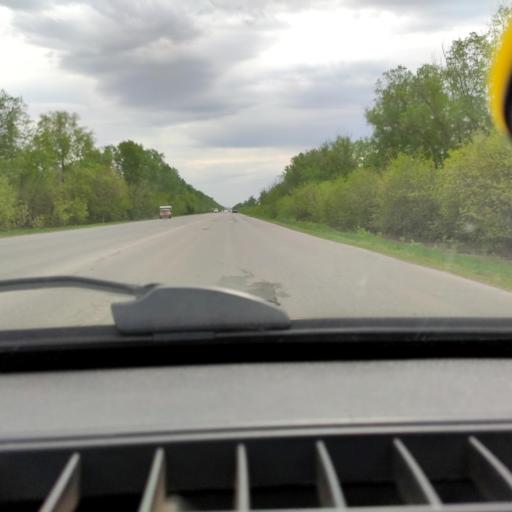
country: RU
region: Samara
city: Tol'yatti
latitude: 53.6155
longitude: 49.4132
